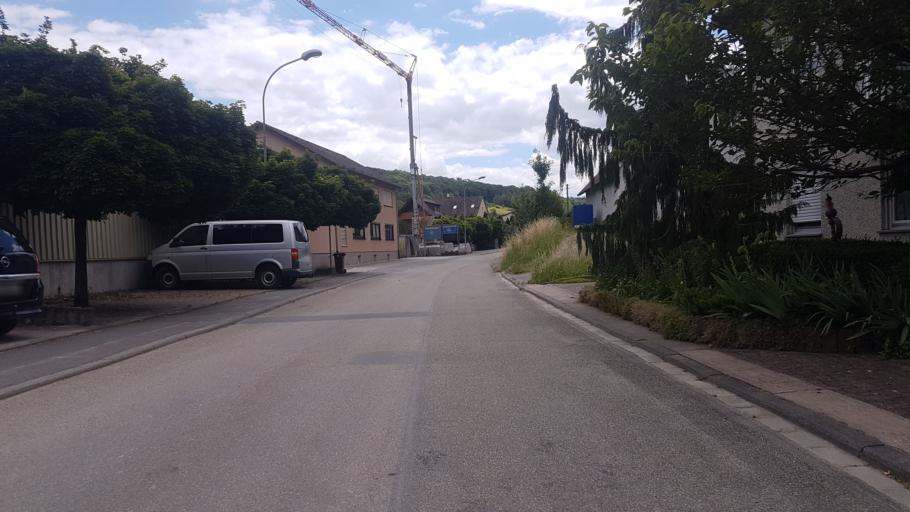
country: DE
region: Baden-Wuerttemberg
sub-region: Regierungsbezirk Stuttgart
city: Bad Mergentheim
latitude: 49.4756
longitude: 9.7694
